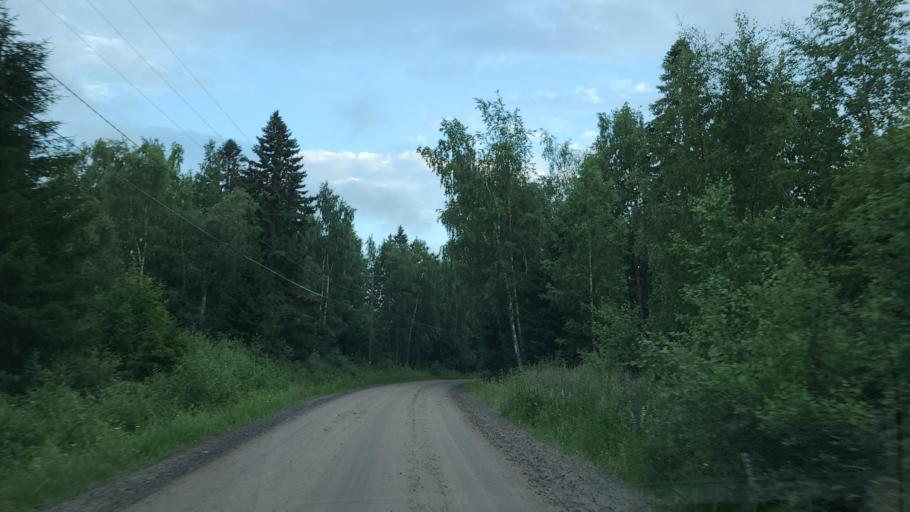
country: FI
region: Ostrobothnia
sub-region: Vaasa
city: Replot
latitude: 63.3096
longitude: 21.1579
